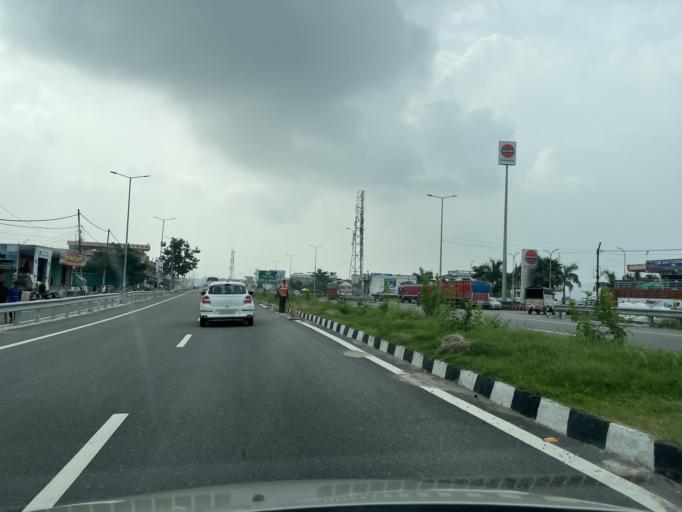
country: IN
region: Uttarakhand
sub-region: Dehradun
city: Raiwala
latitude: 30.0794
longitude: 78.1928
